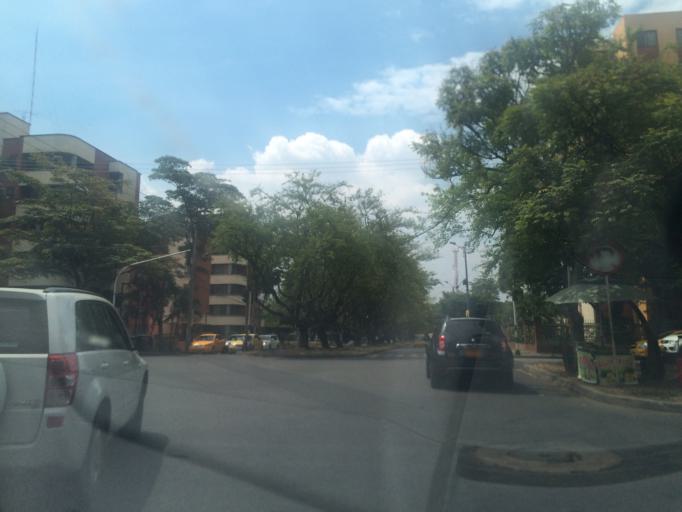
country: CO
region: Valle del Cauca
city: Cali
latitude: 3.3789
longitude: -76.5203
